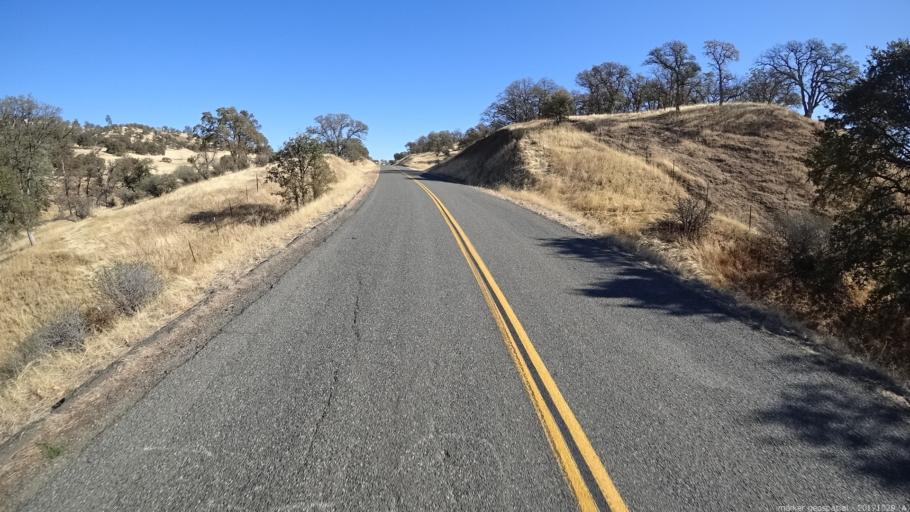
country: US
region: California
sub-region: Shasta County
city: Shasta
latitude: 40.4394
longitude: -122.6607
